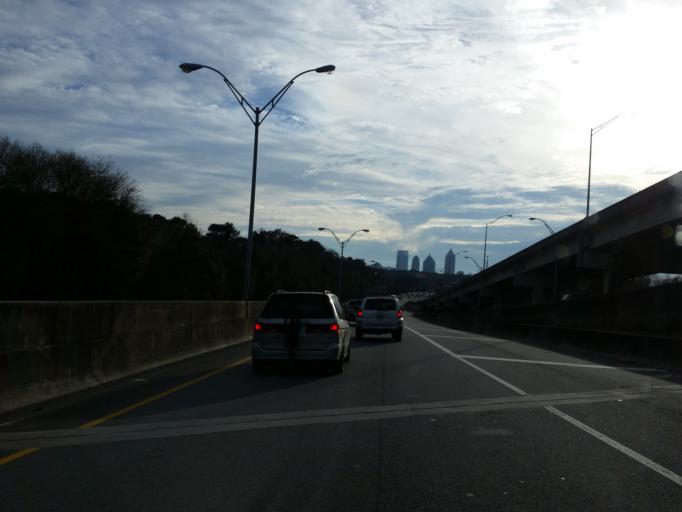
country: US
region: Georgia
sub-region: DeKalb County
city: North Druid Hills
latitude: 33.8206
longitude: -84.3596
